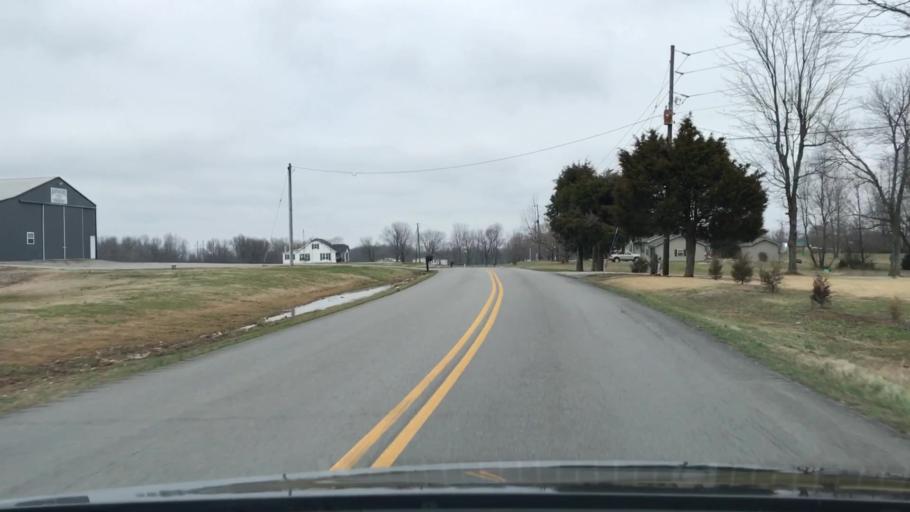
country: US
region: Kentucky
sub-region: Muhlenberg County
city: Morehead
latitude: 37.3349
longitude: -87.2200
